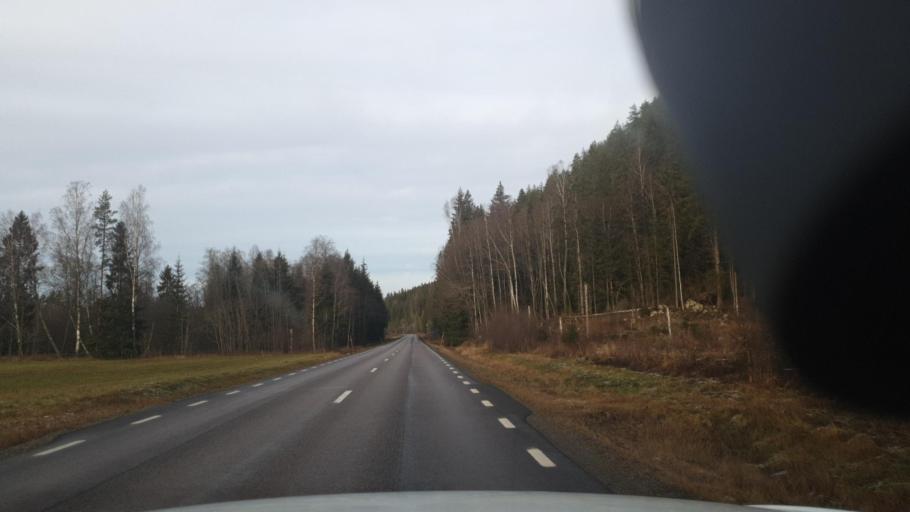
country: SE
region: Vaermland
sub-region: Arjangs Kommun
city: Arjaeng
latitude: 59.6085
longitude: 12.1511
